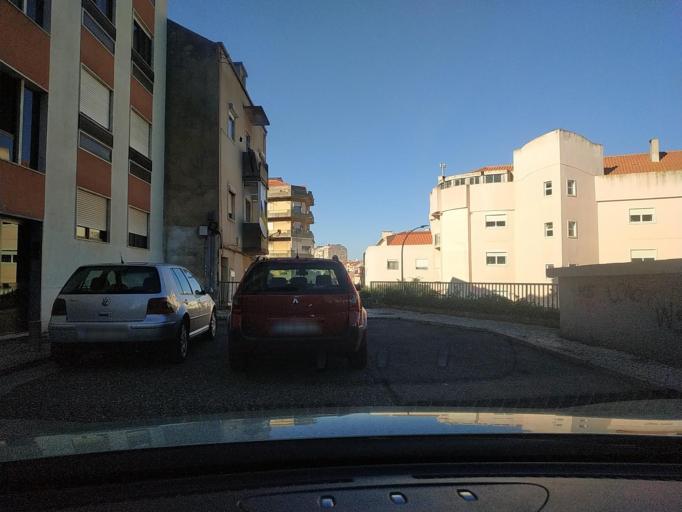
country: PT
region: Lisbon
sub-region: Odivelas
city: Pontinha
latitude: 38.7679
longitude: -9.2171
